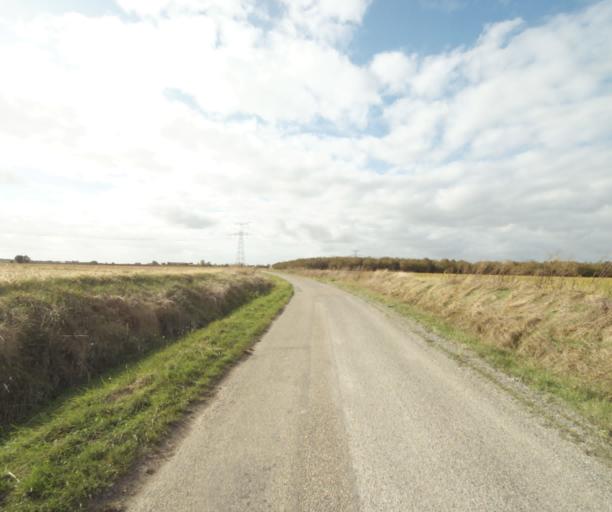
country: FR
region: Midi-Pyrenees
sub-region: Departement du Tarn-et-Garonne
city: Finhan
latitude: 43.8987
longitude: 1.1222
